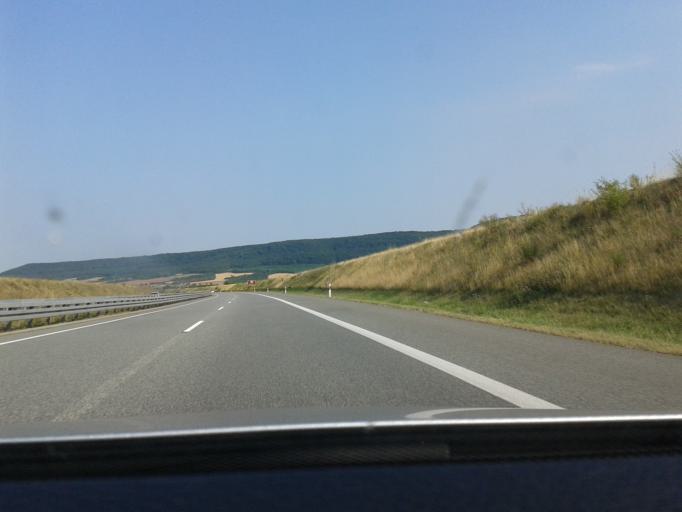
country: DE
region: Thuringia
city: Sollstedt
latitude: 51.4188
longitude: 10.5537
